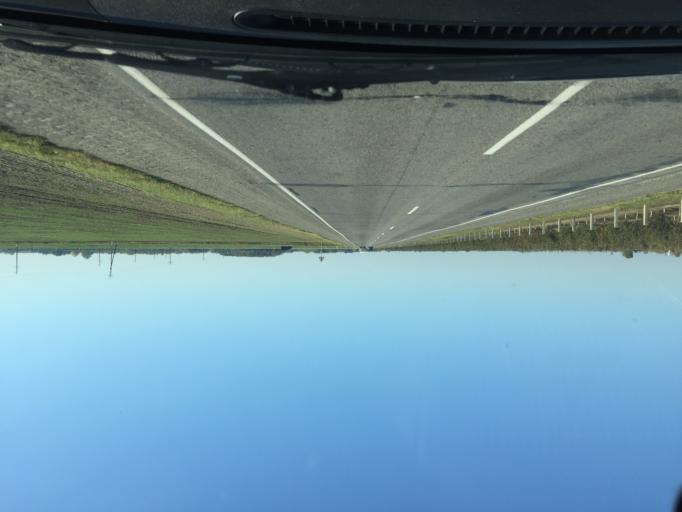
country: BY
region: Gomel
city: Turaw
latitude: 52.0598
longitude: 27.8036
